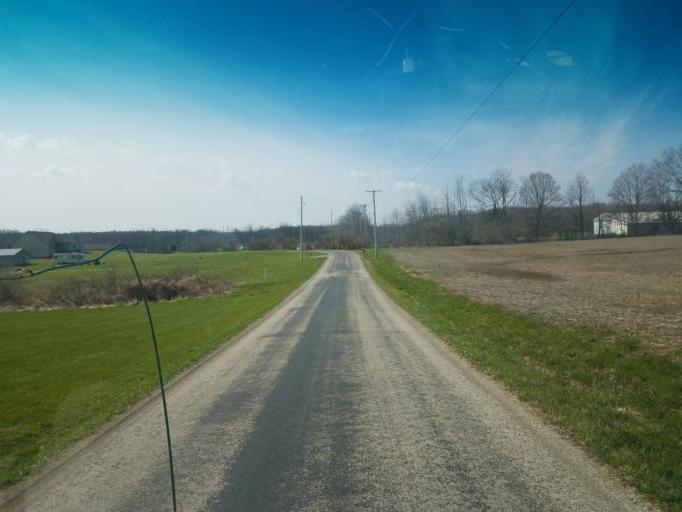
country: US
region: Ohio
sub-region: Richland County
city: Lincoln Heights
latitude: 40.8421
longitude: -82.4942
